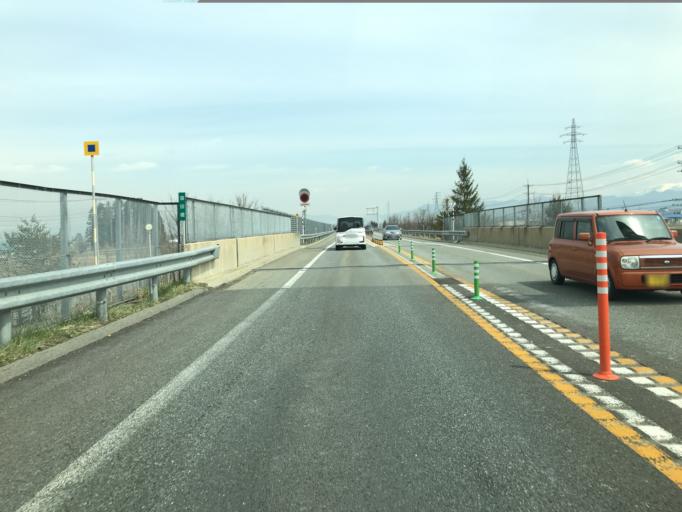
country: JP
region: Yamagata
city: Yonezawa
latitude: 37.9611
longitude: 140.1196
